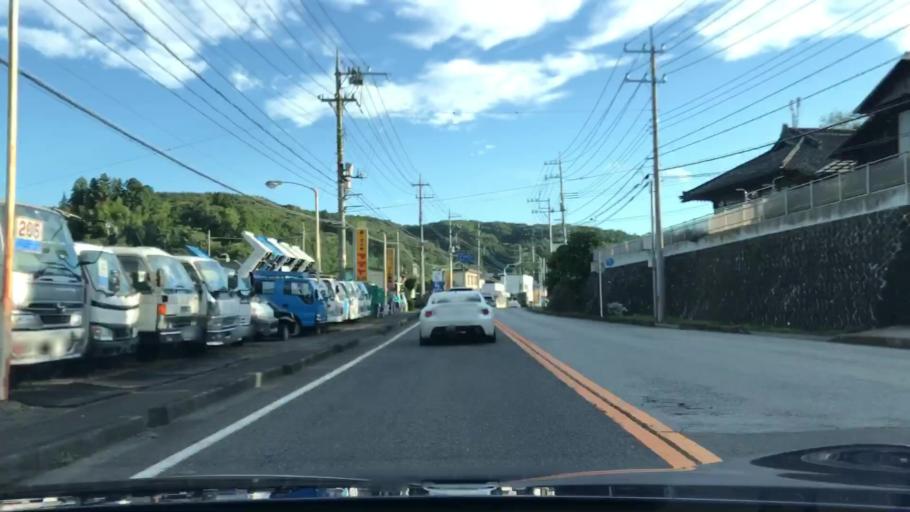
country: JP
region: Tochigi
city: Motegi
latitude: 36.5357
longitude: 140.2062
